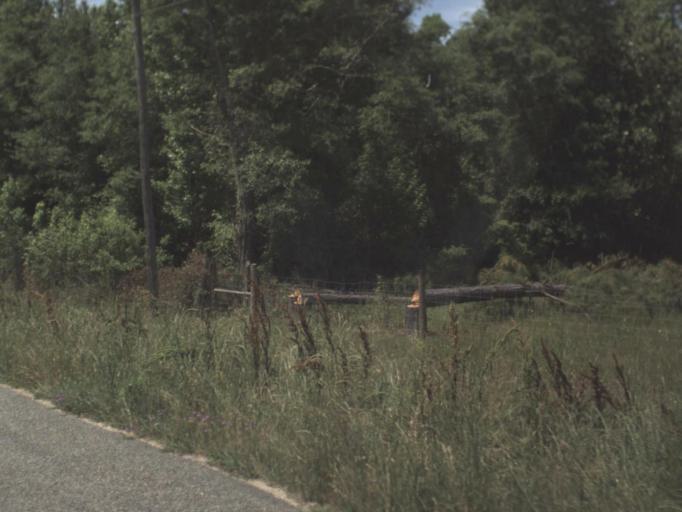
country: US
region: Florida
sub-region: Jackson County
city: Marianna
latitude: 30.7038
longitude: -85.2315
